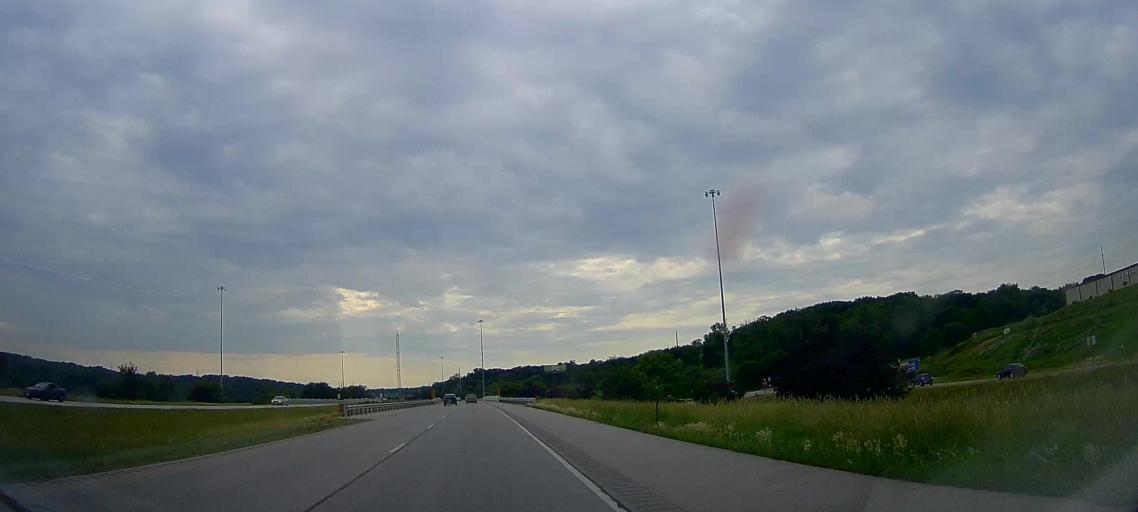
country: US
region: Iowa
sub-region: Pottawattamie County
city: Carter Lake
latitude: 41.3471
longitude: -95.9807
